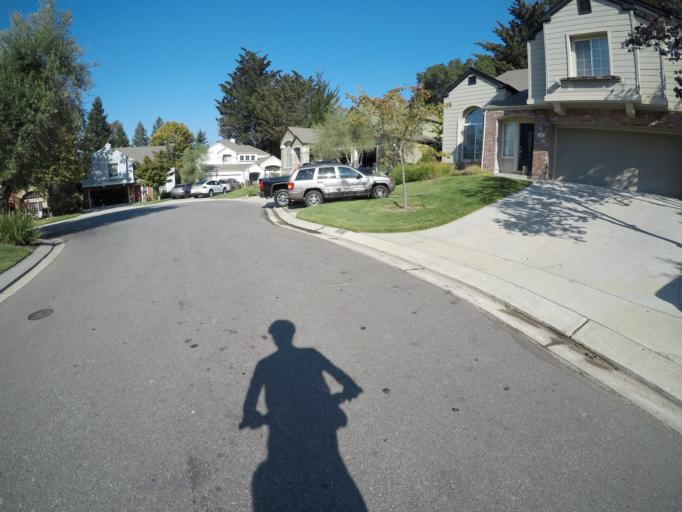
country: US
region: California
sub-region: Santa Cruz County
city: Scotts Valley
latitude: 37.0405
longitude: -122.0155
